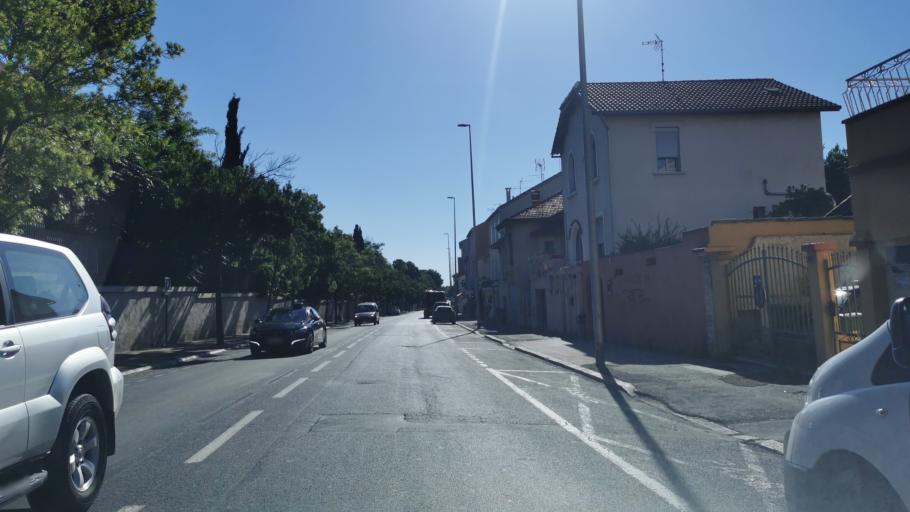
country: FR
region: Languedoc-Roussillon
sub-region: Departement de l'Herault
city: Beziers
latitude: 43.3444
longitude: 3.2306
